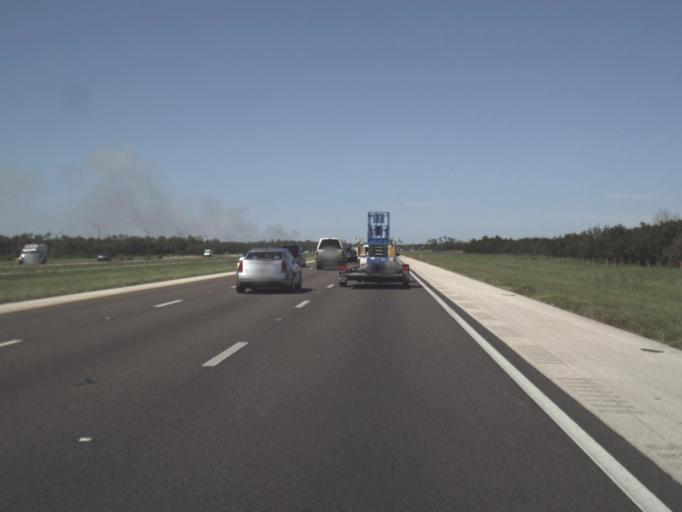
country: US
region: Florida
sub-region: Lee County
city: Bonita Springs
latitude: 26.3646
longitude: -81.7645
